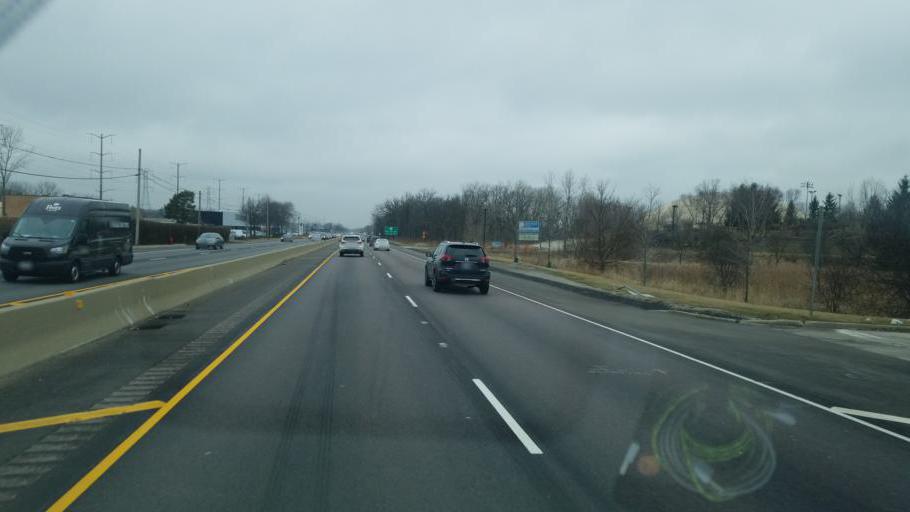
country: US
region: Illinois
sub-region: Lake County
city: Highwood
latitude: 42.1915
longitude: -87.8272
